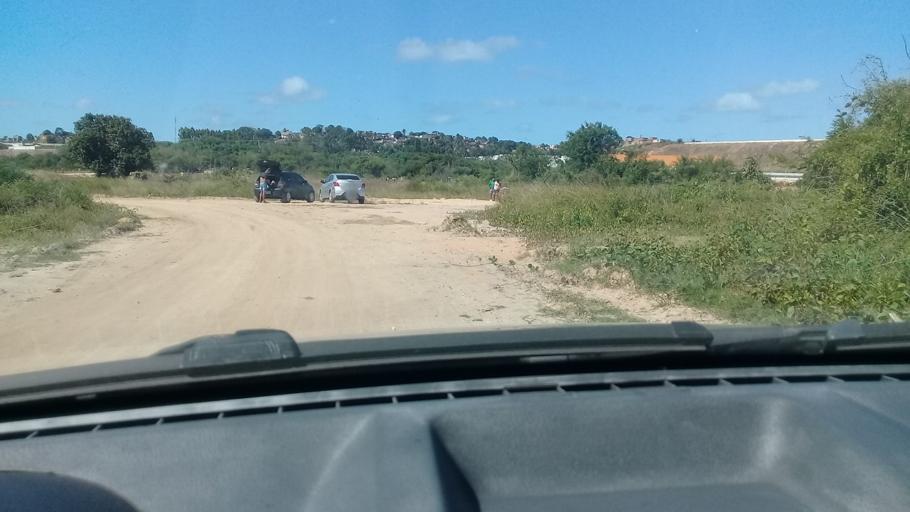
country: BR
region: Pernambuco
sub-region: Jaboatao Dos Guararapes
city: Jaboatao
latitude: -8.1484
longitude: -34.9506
